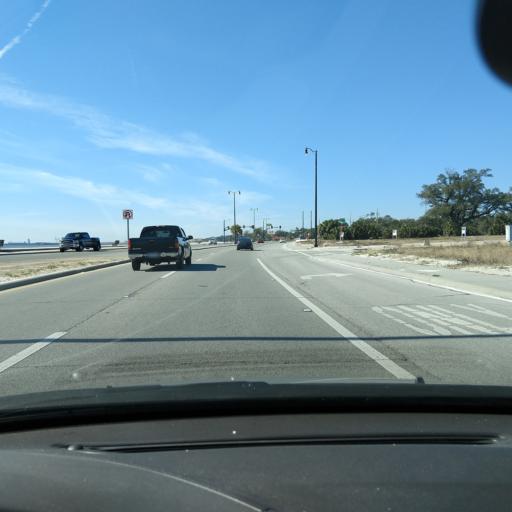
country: US
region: Mississippi
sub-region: Harrison County
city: Gulfport
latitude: 30.3804
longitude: -89.0334
